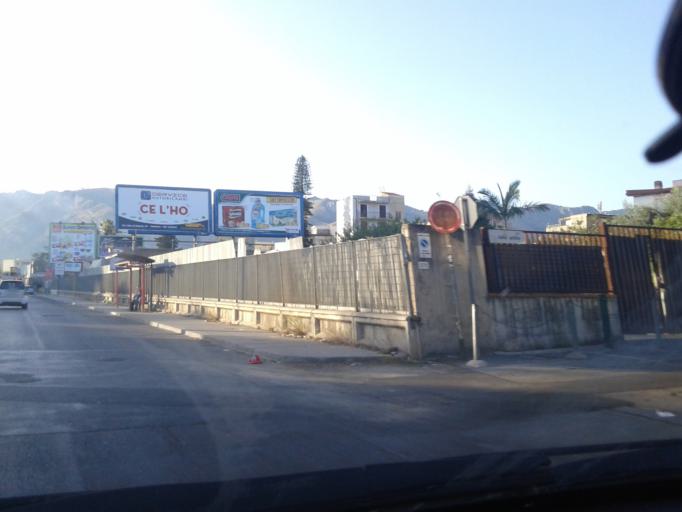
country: IT
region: Sicily
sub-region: Palermo
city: Palermo
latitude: 38.0988
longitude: 13.3326
